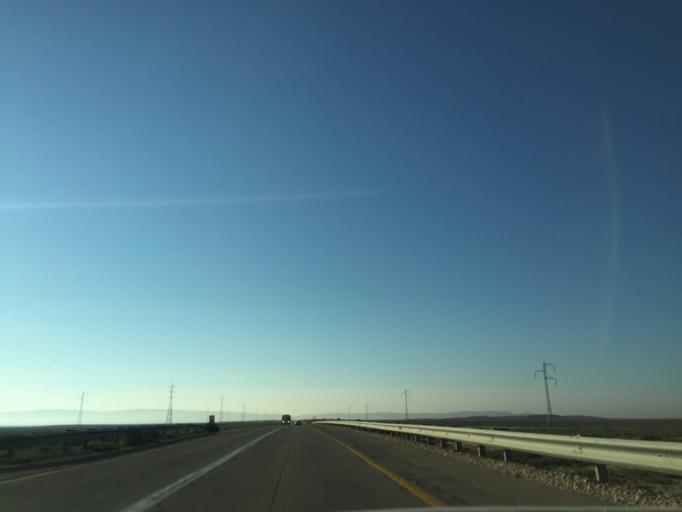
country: IL
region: Southern District
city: Mitzpe Ramon
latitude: 30.4501
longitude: 34.9370
